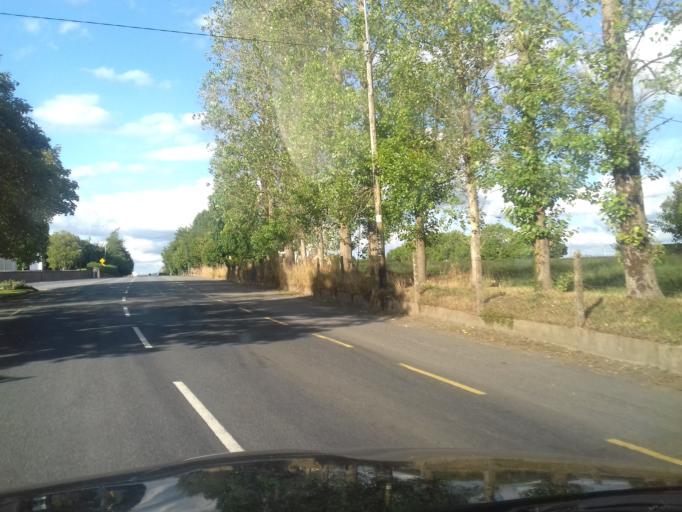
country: IE
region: Leinster
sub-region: Loch Garman
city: New Ross
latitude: 52.4528
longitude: -6.9610
